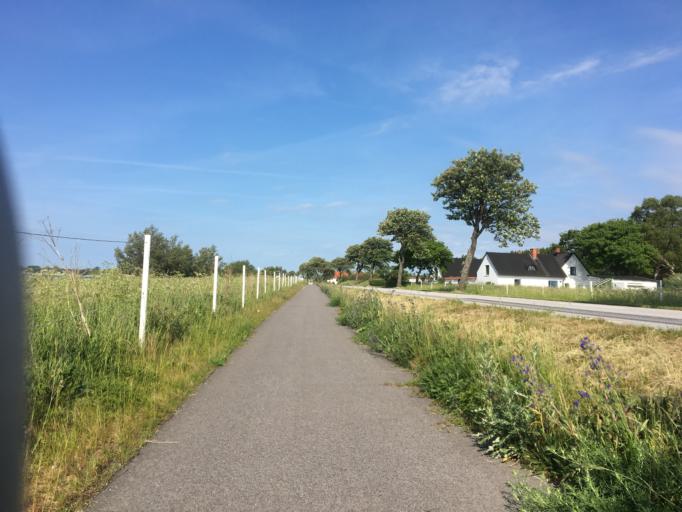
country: SE
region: Skane
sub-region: Skurups Kommun
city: Rydsgard
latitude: 55.4179
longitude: 13.6553
